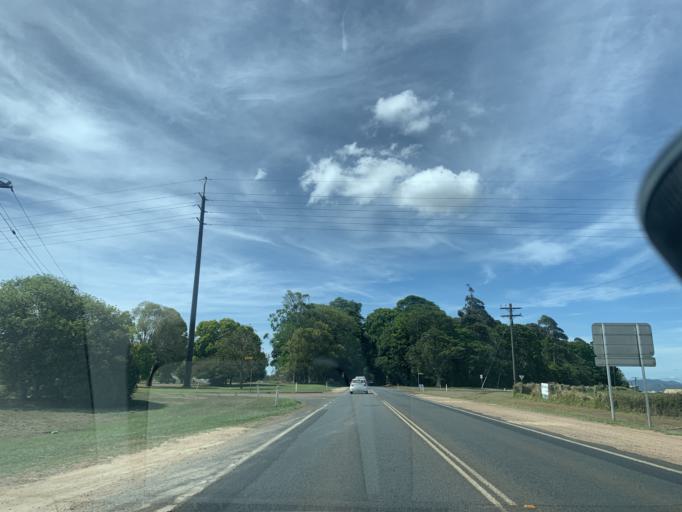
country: AU
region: Queensland
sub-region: Tablelands
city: Tolga
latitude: -17.2465
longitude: 145.4797
